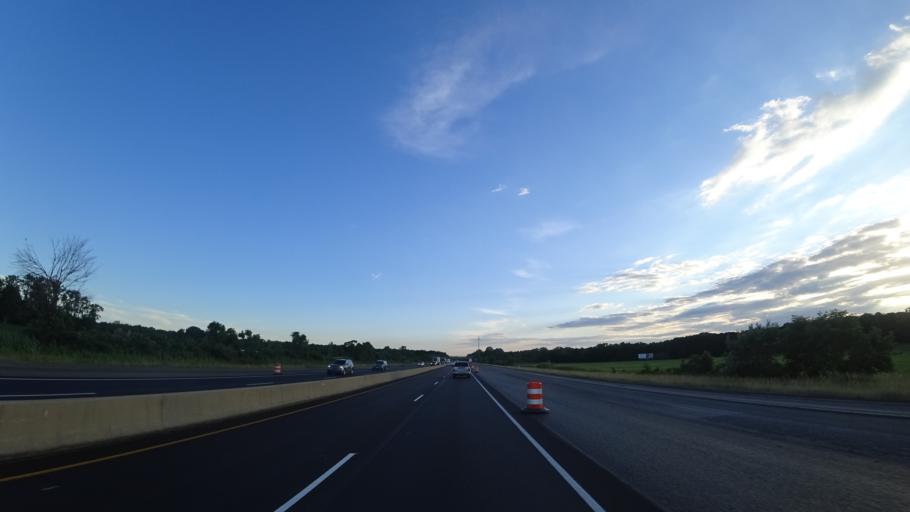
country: US
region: Michigan
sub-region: Berrien County
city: New Buffalo
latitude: 41.7412
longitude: -86.7810
